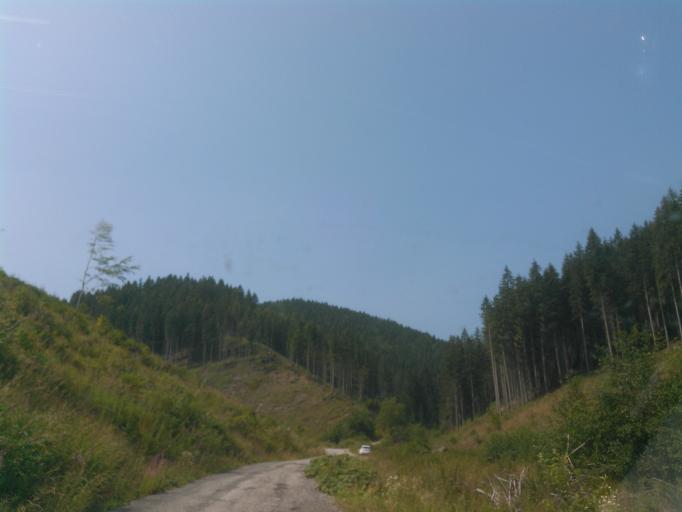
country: SK
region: Zilinsky
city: Ruzomberok
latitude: 48.9584
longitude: 19.3975
